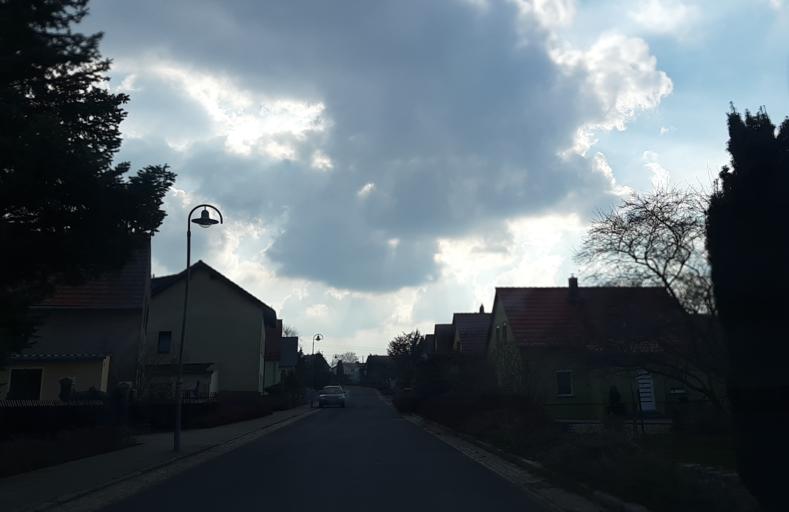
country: DE
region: Saxony
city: Wildenhain
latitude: 51.2883
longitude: 13.4738
